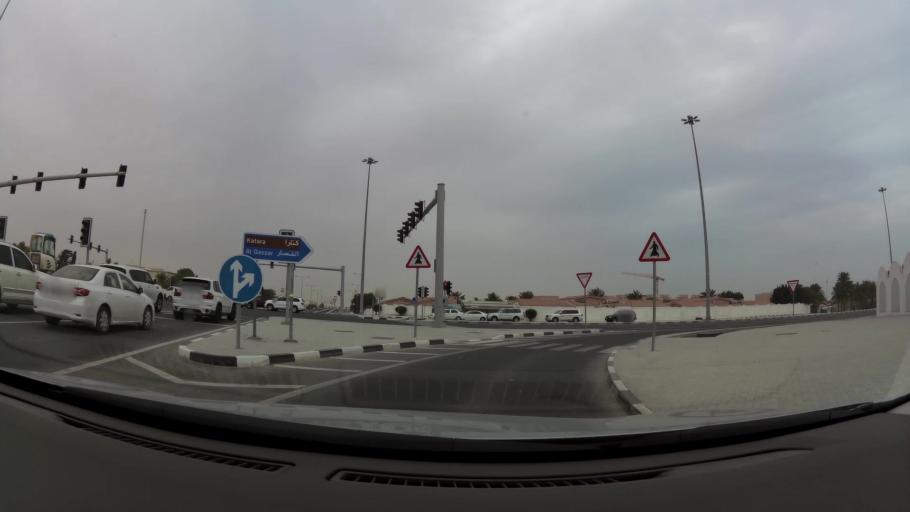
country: QA
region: Baladiyat ar Rayyan
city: Ar Rayyan
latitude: 25.3474
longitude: 51.4679
